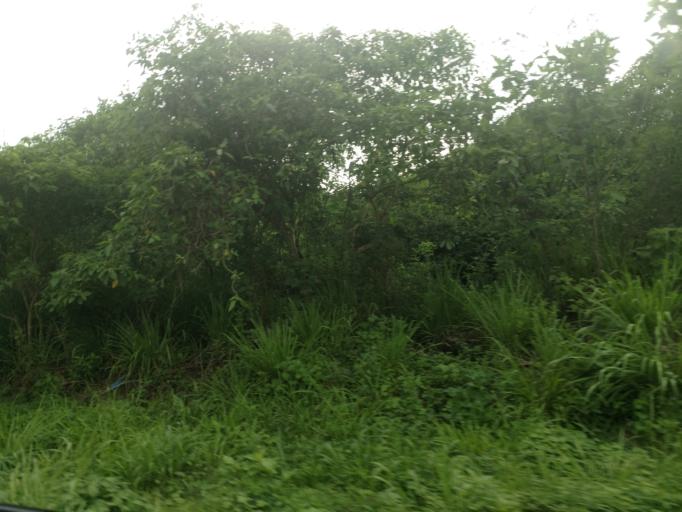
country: MX
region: Nayarit
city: Xalisco
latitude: 21.4772
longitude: -104.8590
